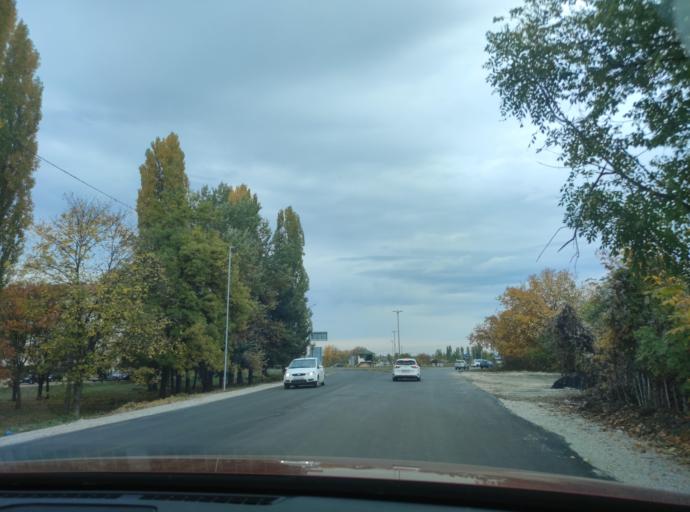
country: BG
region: Montana
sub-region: Obshtina Montana
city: Montana
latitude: 43.4010
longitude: 23.2400
